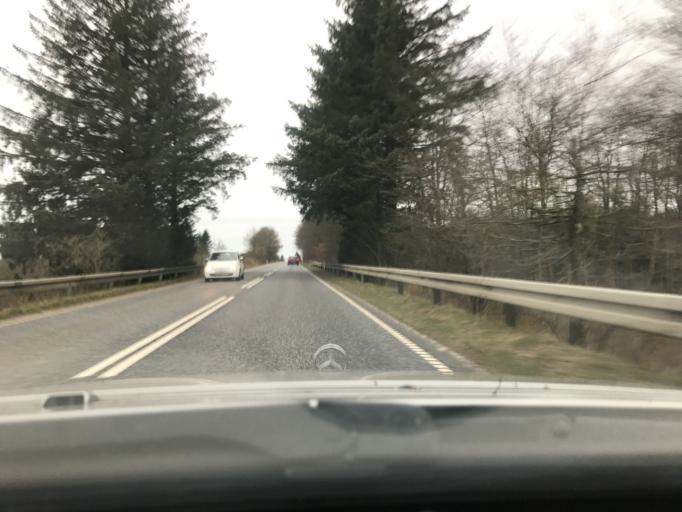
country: DK
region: South Denmark
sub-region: Tonder Kommune
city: Logumkloster
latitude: 55.1698
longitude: 8.9599
